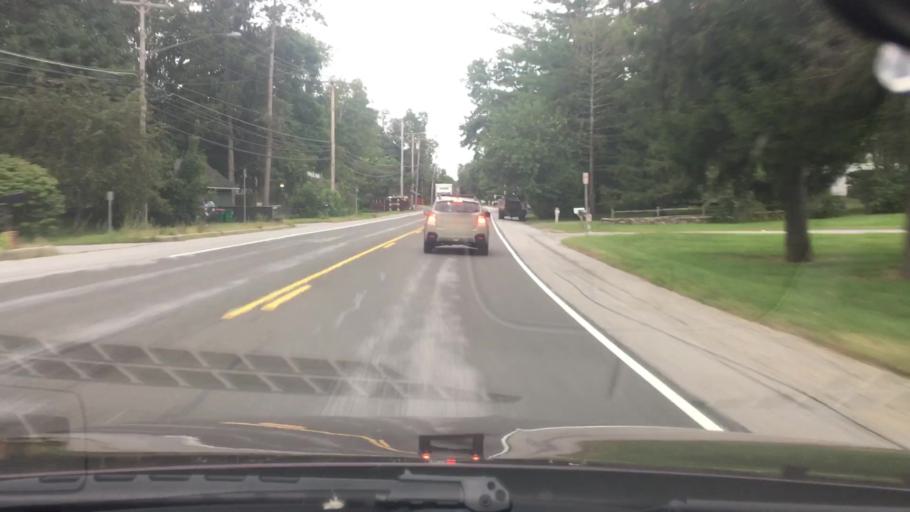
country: US
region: New York
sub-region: Dutchess County
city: Pleasant Valley
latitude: 41.7362
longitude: -73.8348
